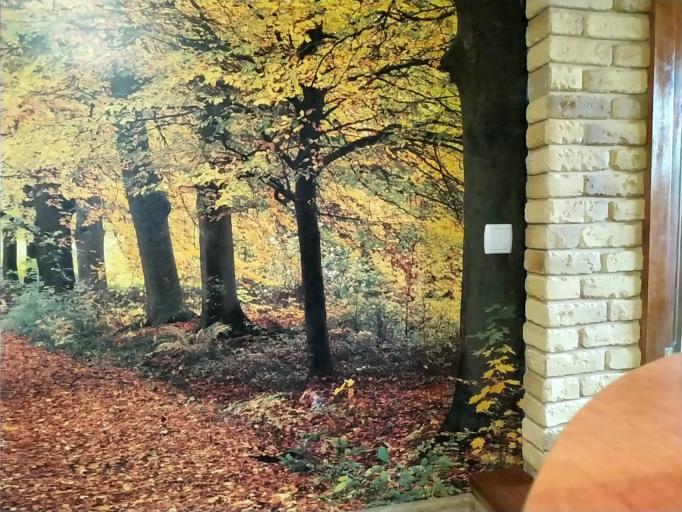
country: RU
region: Leningrad
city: Tolmachevo
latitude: 58.9422
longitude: 29.6675
